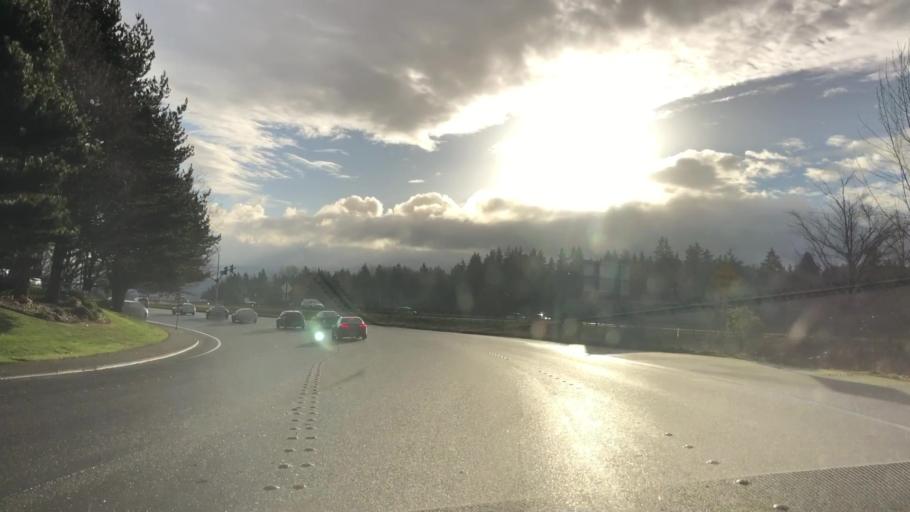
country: US
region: Washington
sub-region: King County
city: Eastgate
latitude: 47.5797
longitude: -122.1364
